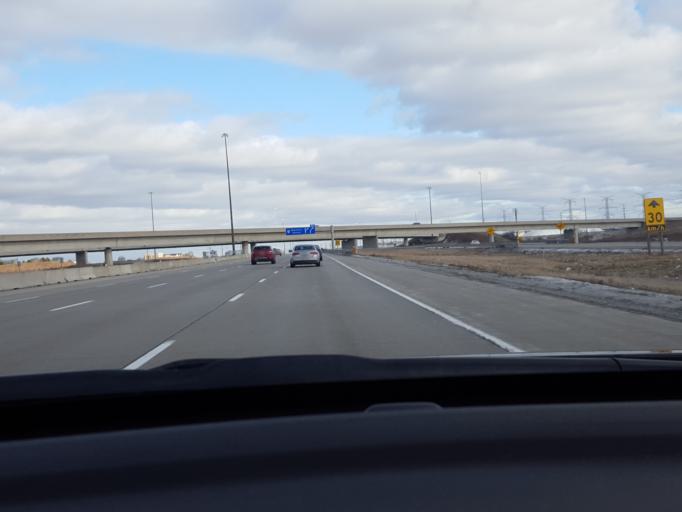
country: CA
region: Ontario
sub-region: York
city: Richmond Hill
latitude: 43.8381
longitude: -79.3728
